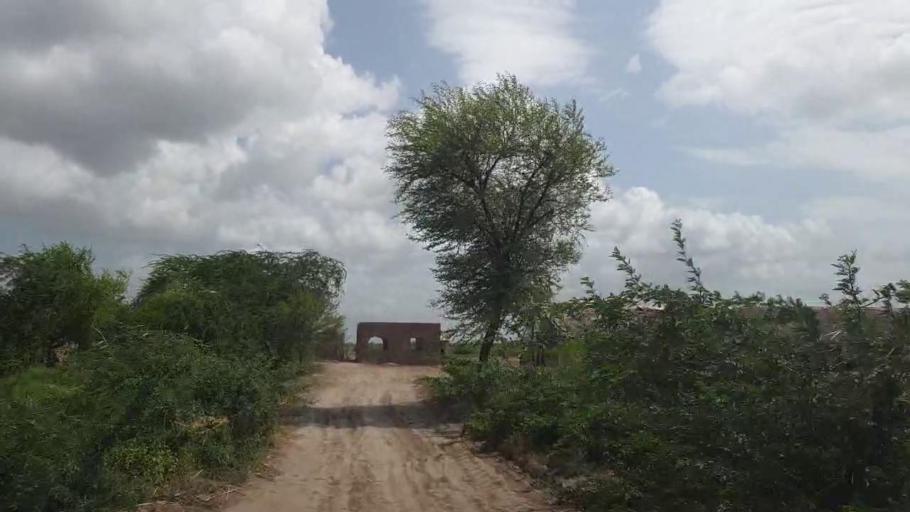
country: PK
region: Sindh
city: Tando Bago
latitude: 24.6499
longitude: 68.9979
